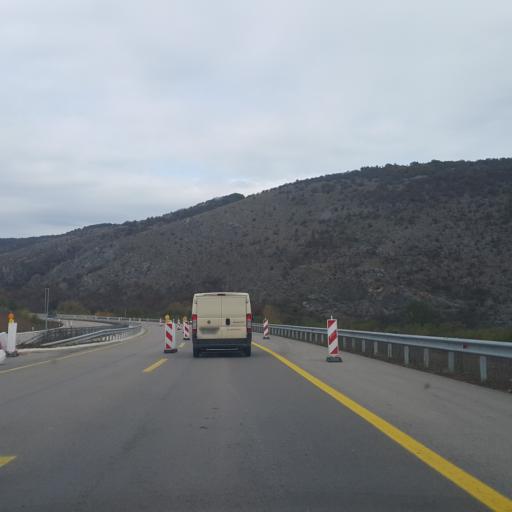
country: RS
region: Central Serbia
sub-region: Pirotski Okrug
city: Bela Palanka
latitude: 43.2315
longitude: 22.3796
